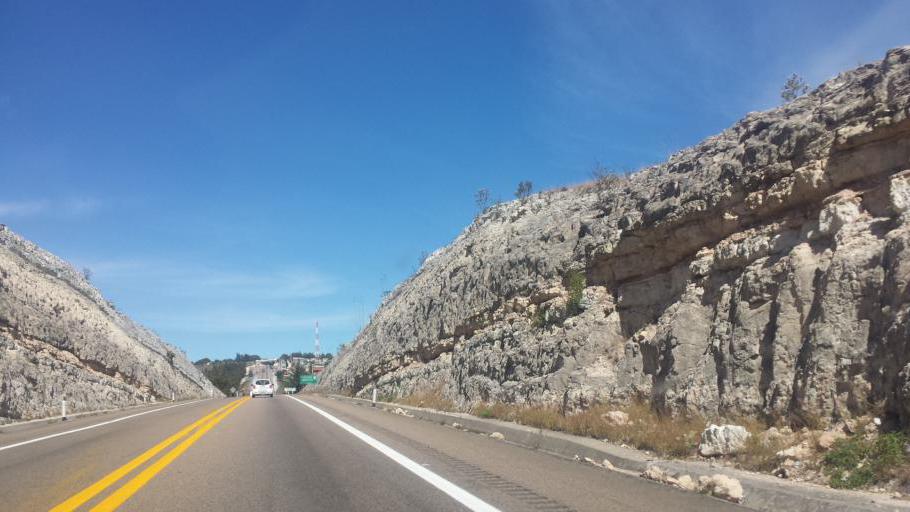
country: MX
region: Oaxaca
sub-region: Villa Tejupam de la Union
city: Villa Tejupam de la Union
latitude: 17.8732
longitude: -97.3754
